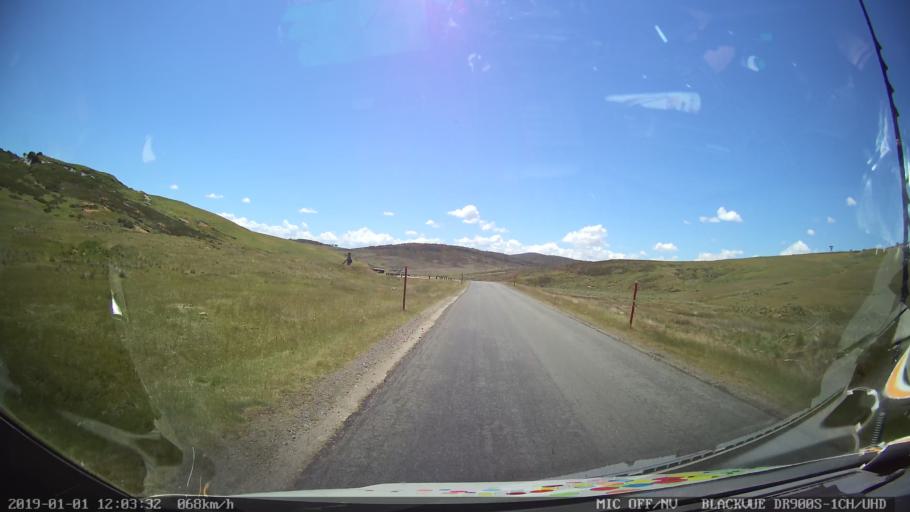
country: AU
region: New South Wales
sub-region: Snowy River
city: Jindabyne
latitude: -35.8696
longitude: 148.4883
